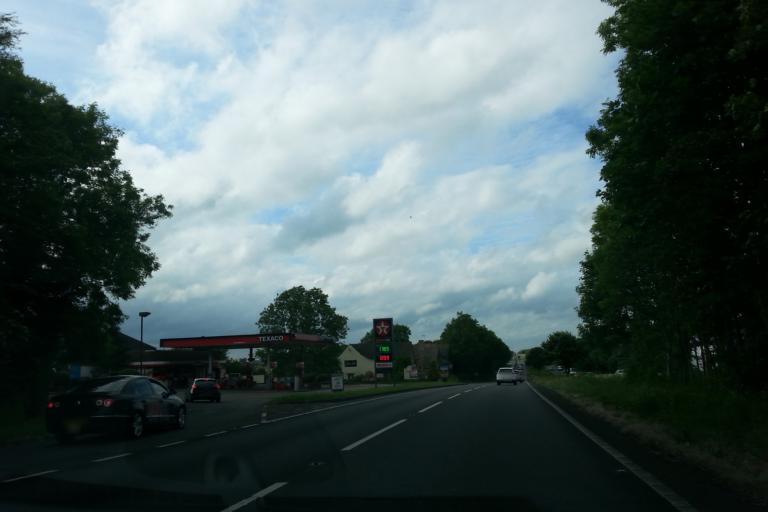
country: GB
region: England
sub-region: District of Rutland
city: Greetham
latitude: 52.7319
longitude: -0.5995
